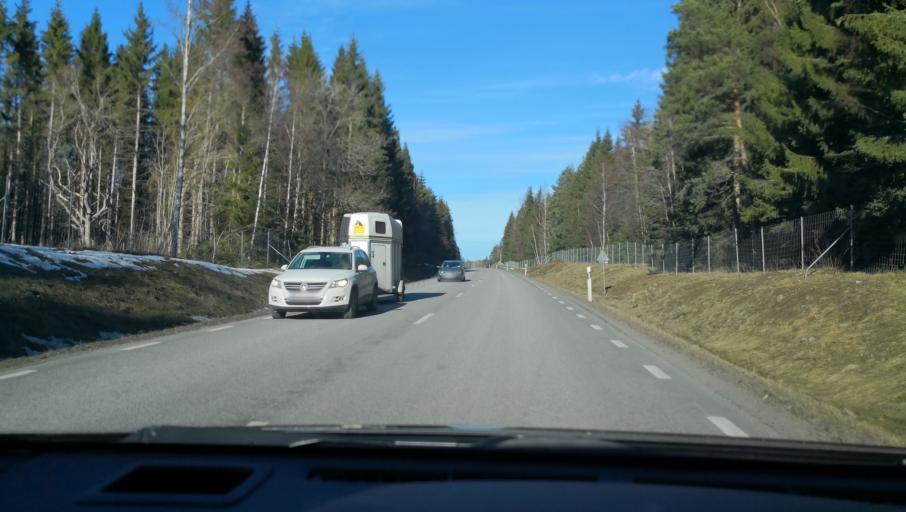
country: SE
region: Uppsala
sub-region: Uppsala Kommun
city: Vattholma
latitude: 60.0307
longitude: 17.7502
